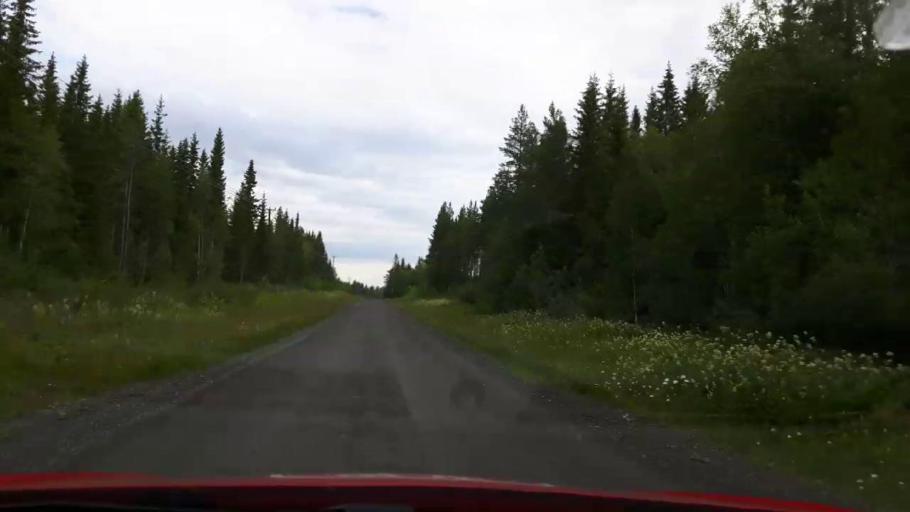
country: SE
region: Jaemtland
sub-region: Stroemsunds Kommun
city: Stroemsund
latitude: 63.5113
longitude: 15.3410
